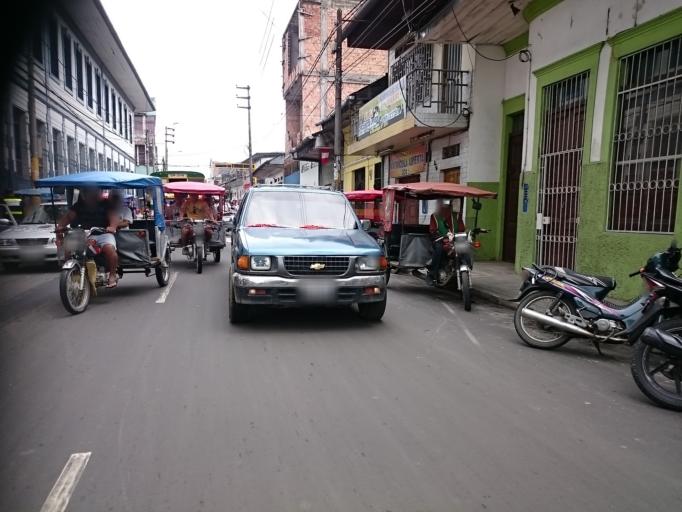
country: PE
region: Loreto
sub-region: Provincia de Maynas
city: Iquitos
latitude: -3.7495
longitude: -73.2465
